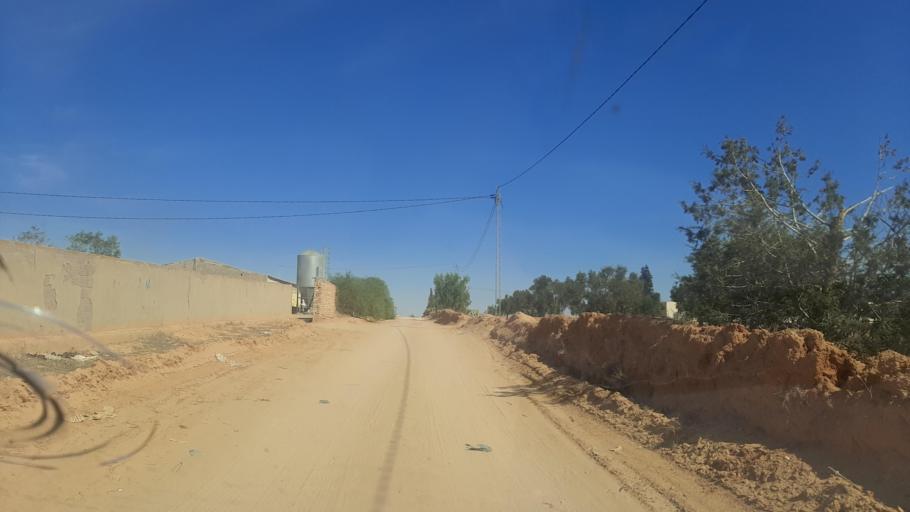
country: TN
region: Safaqis
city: Sfax
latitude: 34.8774
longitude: 10.5706
